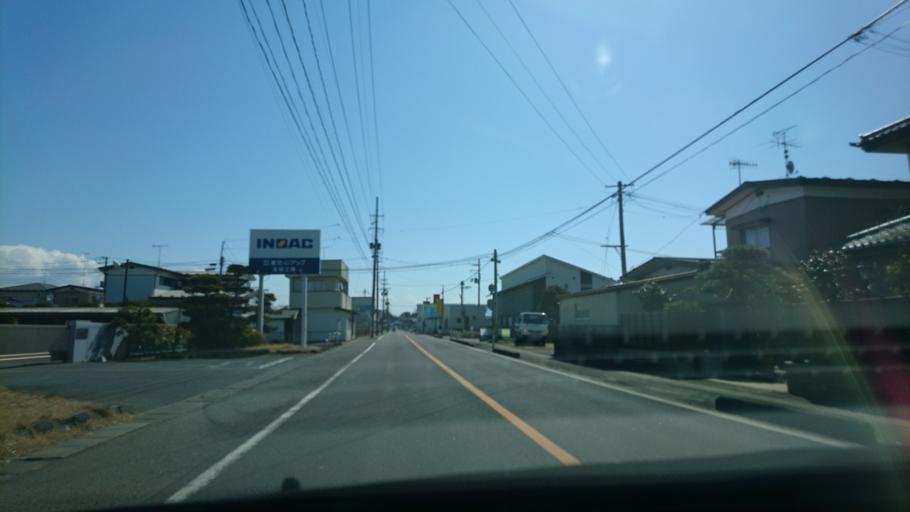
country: JP
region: Iwate
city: Ichinoseki
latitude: 38.7701
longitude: 141.1518
